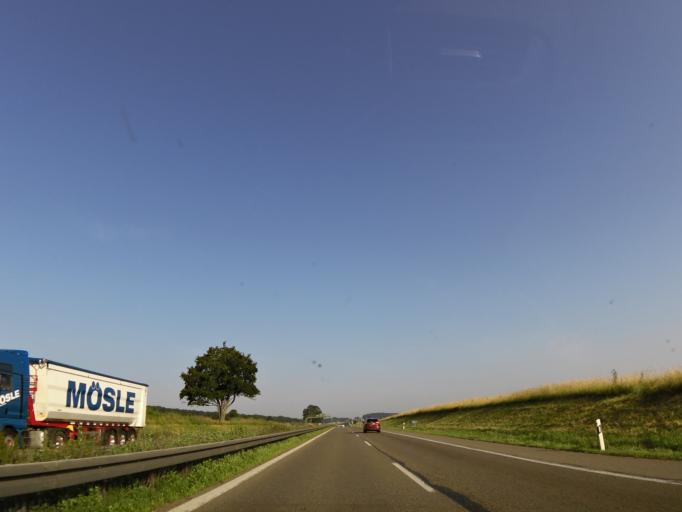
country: DE
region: Baden-Wuerttemberg
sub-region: Tuebingen Region
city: Merklingen
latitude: 48.5199
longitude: 9.7470
